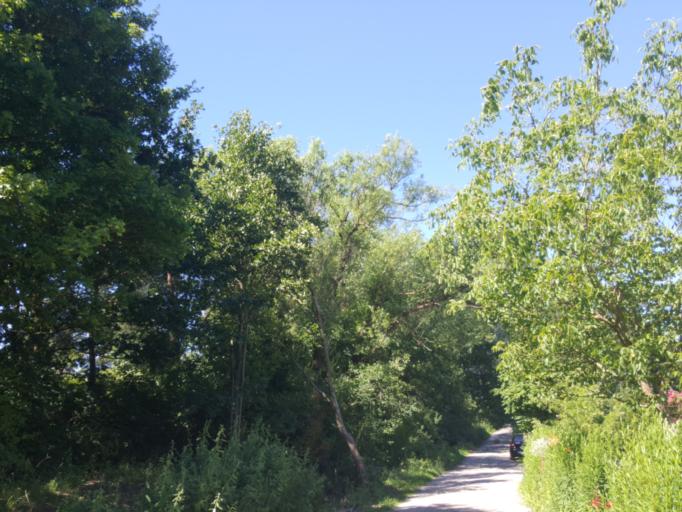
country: DE
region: Hamburg
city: Bergedorf
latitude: 53.4763
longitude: 10.2081
